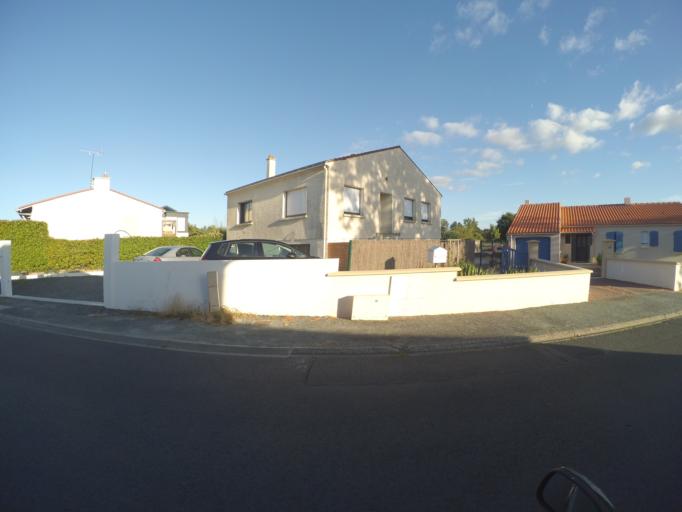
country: FR
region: Pays de la Loire
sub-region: Departement de la Vendee
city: Saint-Hilaire-de-Loulay
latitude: 47.0006
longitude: -1.3337
